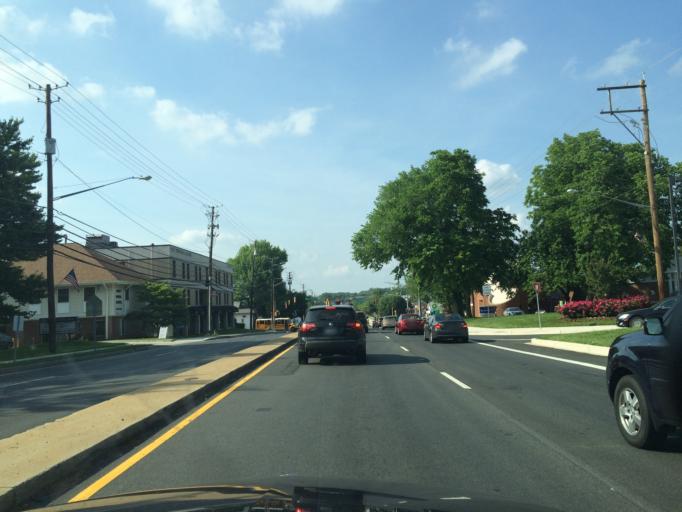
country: US
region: Maryland
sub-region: Montgomery County
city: Olney
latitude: 39.1492
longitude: -77.0668
